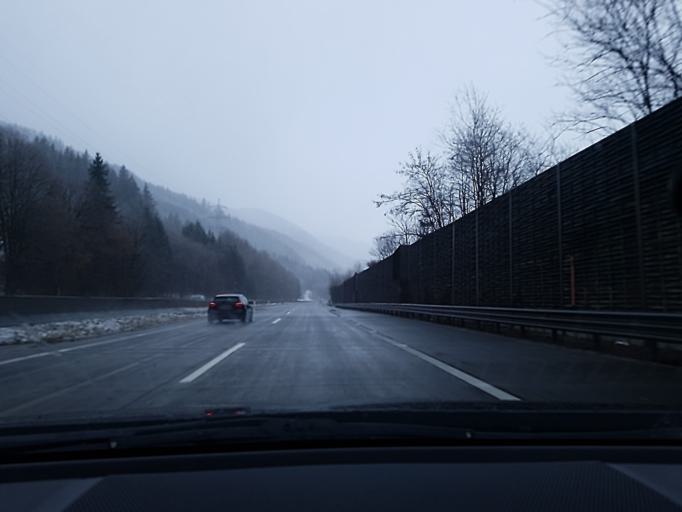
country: AT
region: Salzburg
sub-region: Politischer Bezirk Hallein
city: Kuchl
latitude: 47.6239
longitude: 13.1364
